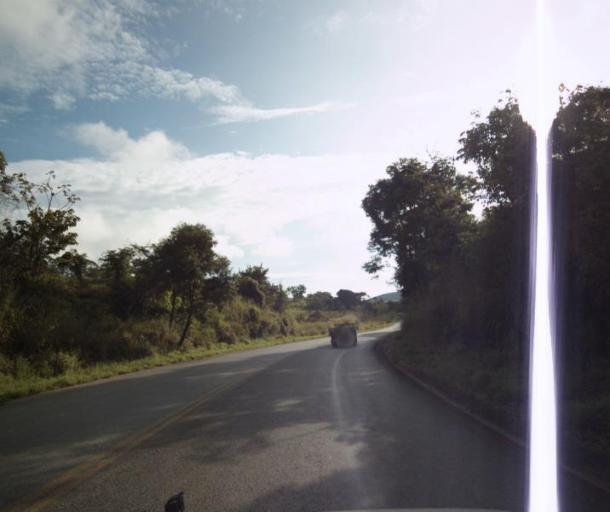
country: BR
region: Goias
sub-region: Pirenopolis
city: Pirenopolis
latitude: -15.7112
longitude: -48.6938
